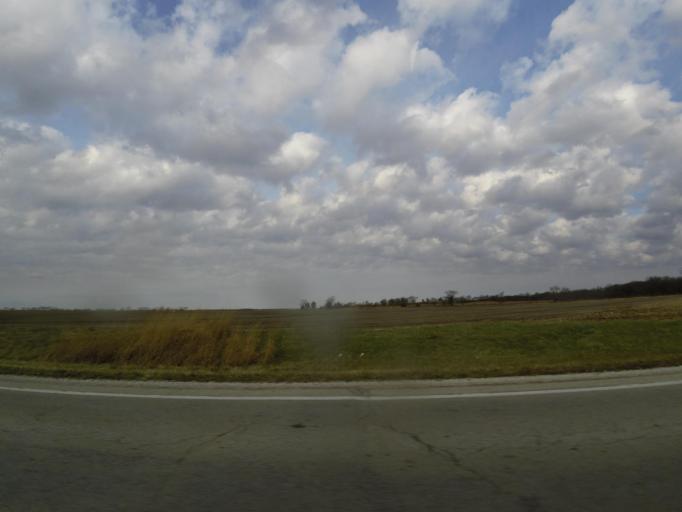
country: US
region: Illinois
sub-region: Christian County
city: Pana
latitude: 39.2954
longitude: -89.0953
